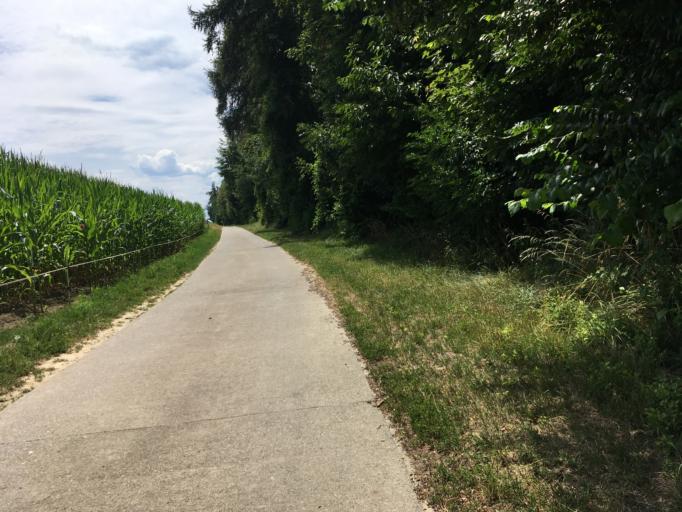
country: CH
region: Vaud
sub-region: Broye-Vully District
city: Payerne
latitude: 46.8978
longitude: 6.9247
